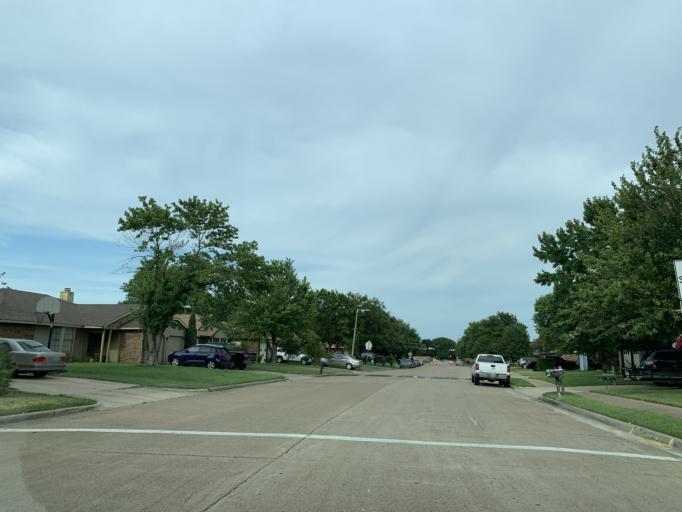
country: US
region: Texas
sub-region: Dallas County
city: Grand Prairie
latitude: 32.6626
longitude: -97.0447
